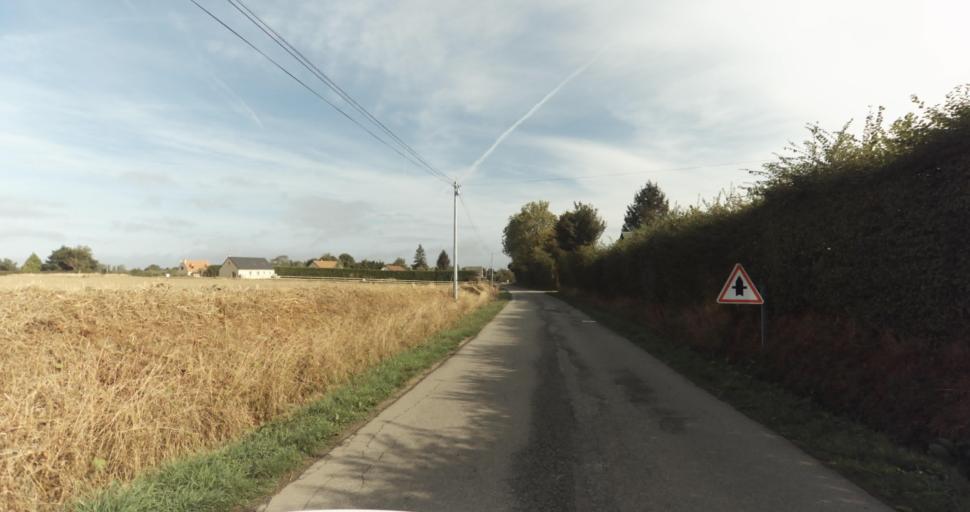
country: FR
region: Lower Normandy
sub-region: Departement de l'Orne
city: Gace
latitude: 48.8878
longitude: 0.3361
